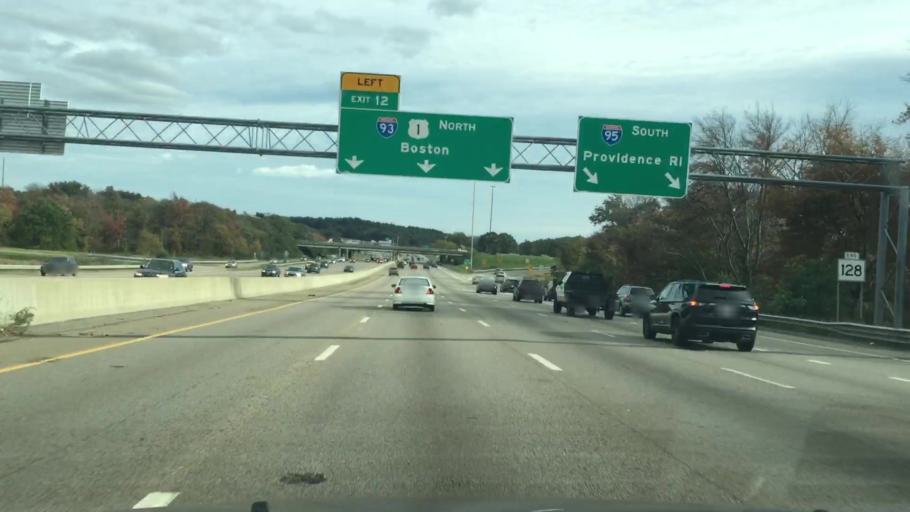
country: US
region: Massachusetts
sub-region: Norfolk County
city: Dedham
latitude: 42.2099
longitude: -71.1444
